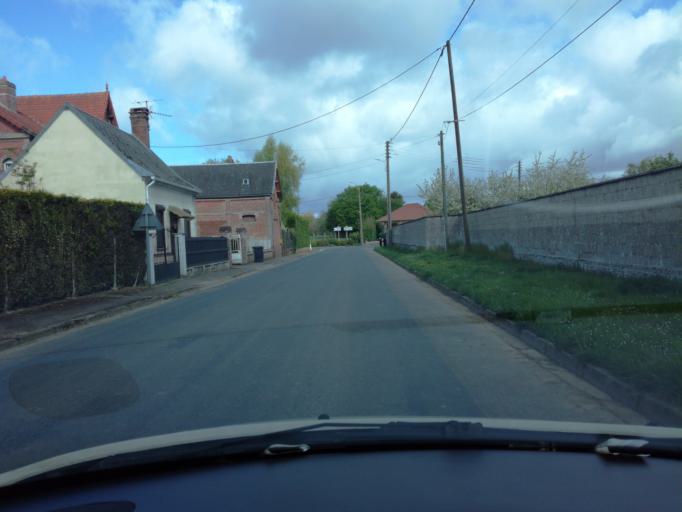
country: FR
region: Picardie
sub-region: Departement de la Somme
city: Hornoy-le-Bourg
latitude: 49.8443
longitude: 1.9034
